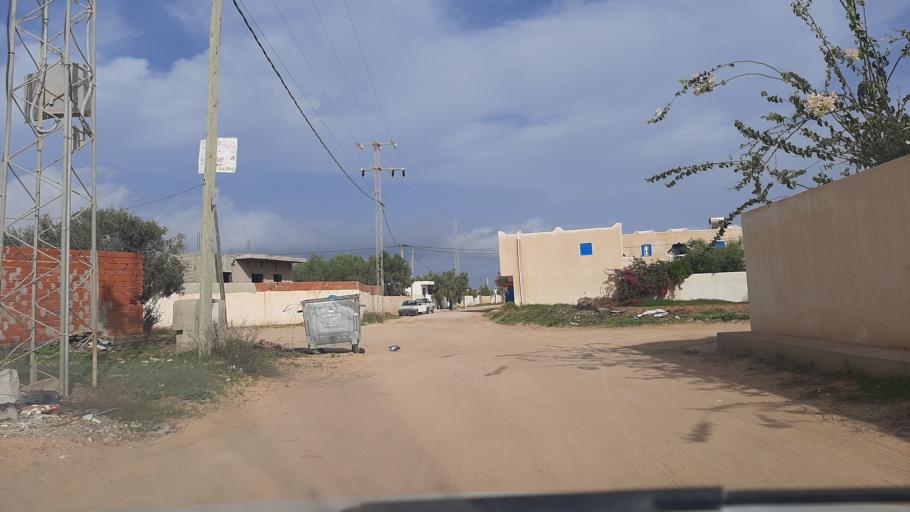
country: TN
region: Madanin
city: Midoun
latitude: 33.8133
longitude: 11.0254
